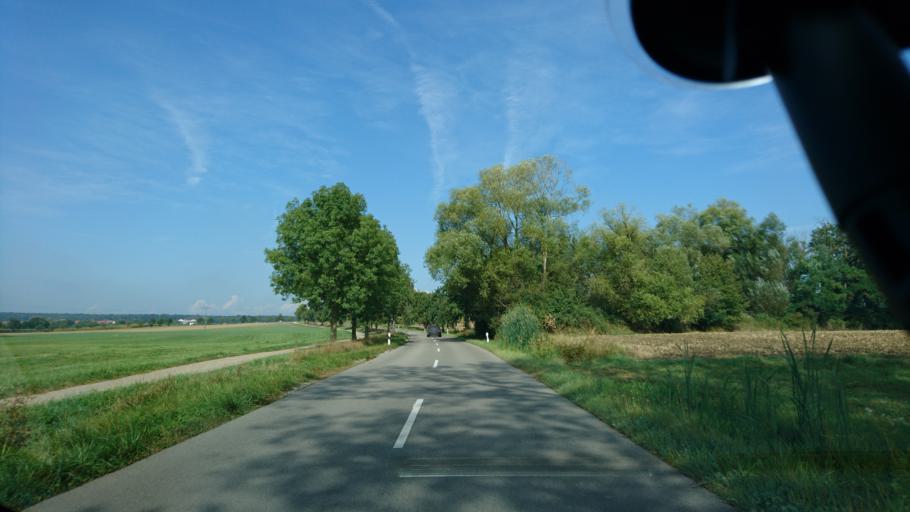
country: DE
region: Baden-Wuerttemberg
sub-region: Regierungsbezirk Stuttgart
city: Ilshofen
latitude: 49.1576
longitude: 9.9298
